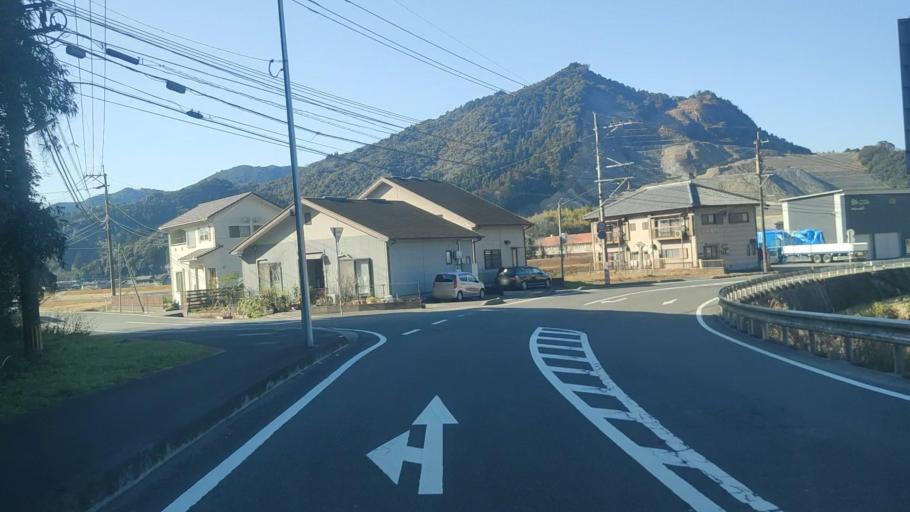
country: JP
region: Oita
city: Saiki
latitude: 32.9769
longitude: 131.8522
